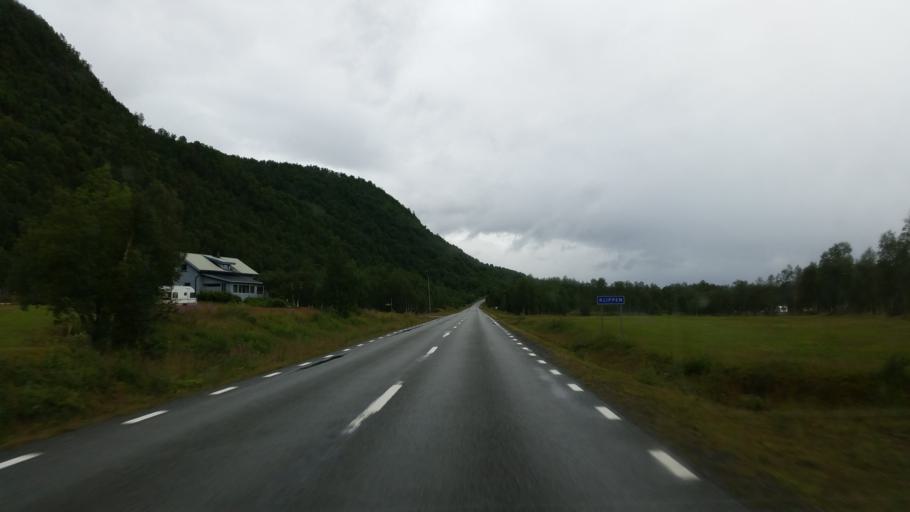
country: NO
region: Nordland
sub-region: Rana
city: Mo i Rana
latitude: 65.8795
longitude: 14.9961
